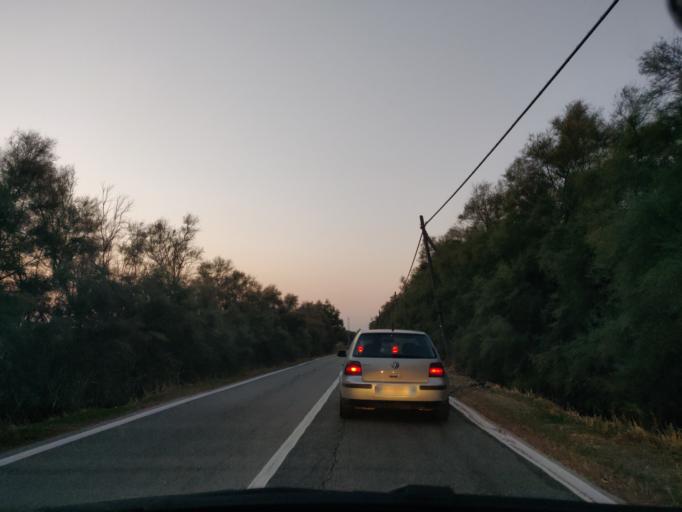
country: IT
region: Latium
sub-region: Citta metropolitana di Roma Capitale
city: Npp 23 (Parco Leonardo)
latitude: 41.8227
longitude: 12.2921
